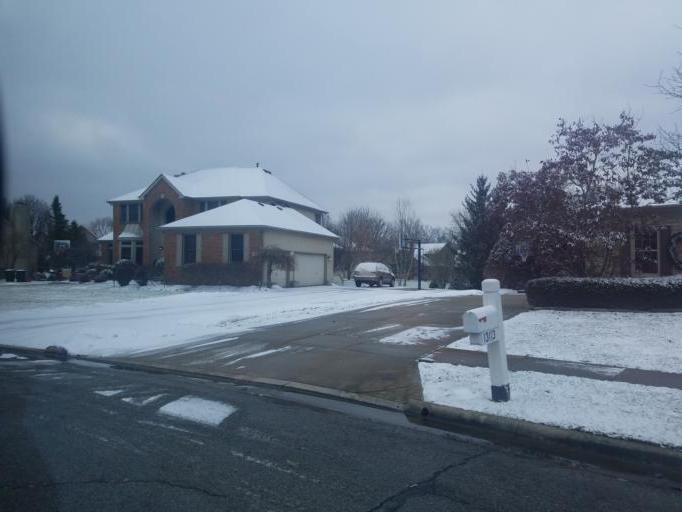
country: US
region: Ohio
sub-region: Franklin County
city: New Albany
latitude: 40.0521
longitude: -82.8329
